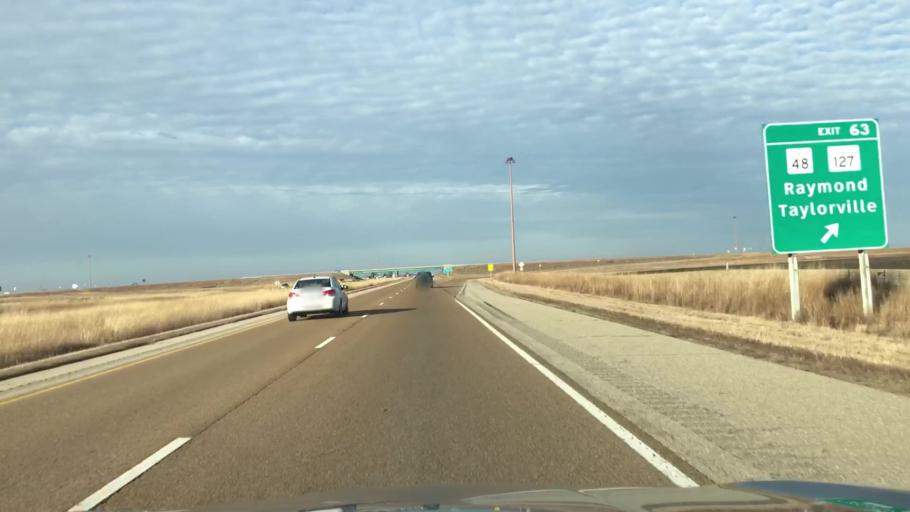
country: US
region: Illinois
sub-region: Montgomery County
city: Raymond
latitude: 39.3165
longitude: -89.6424
